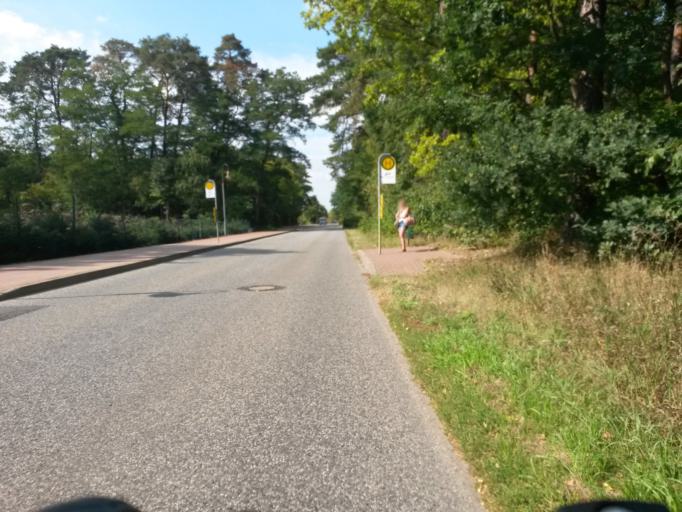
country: DE
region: Brandenburg
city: Templin
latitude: 53.1057
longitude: 13.5235
